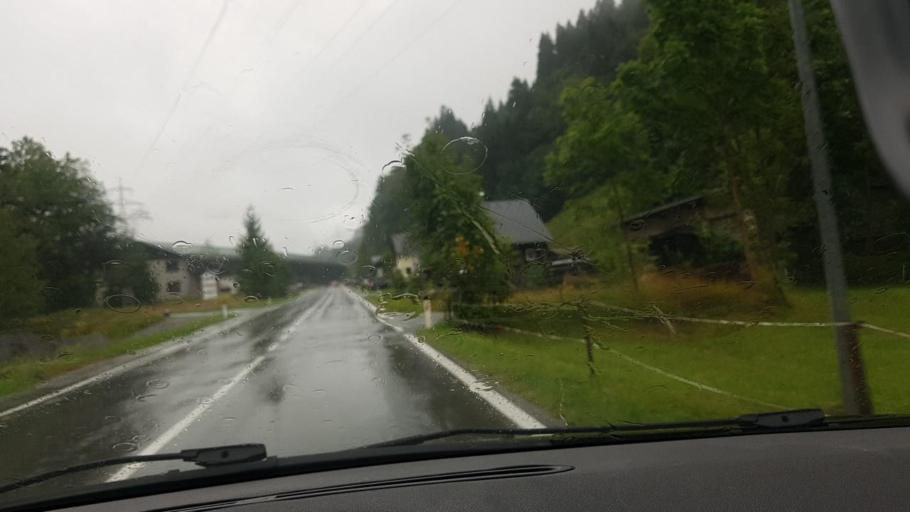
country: AT
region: Vorarlberg
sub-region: Politischer Bezirk Bludenz
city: Dalaas
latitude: 47.1239
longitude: 10.0107
